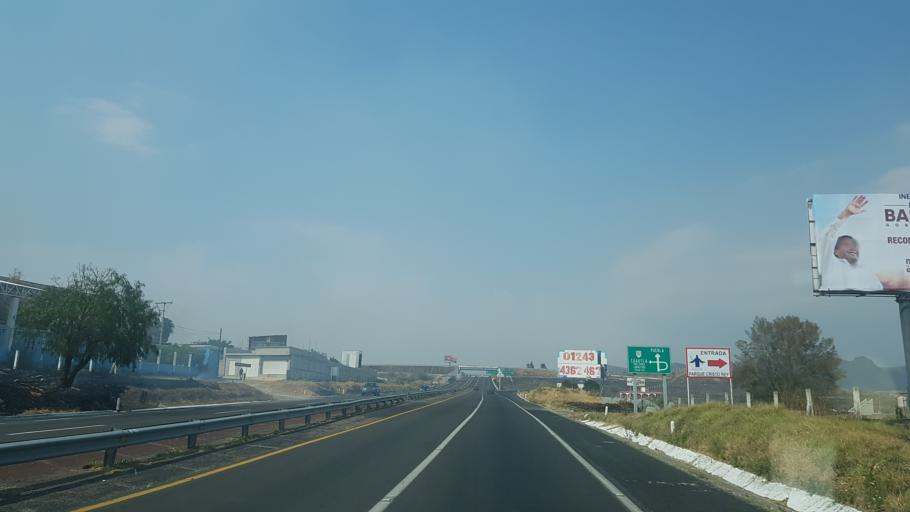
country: MX
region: Puebla
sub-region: Atlixco
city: San Agustin Huixaxtla
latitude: 18.9327
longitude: -98.3944
